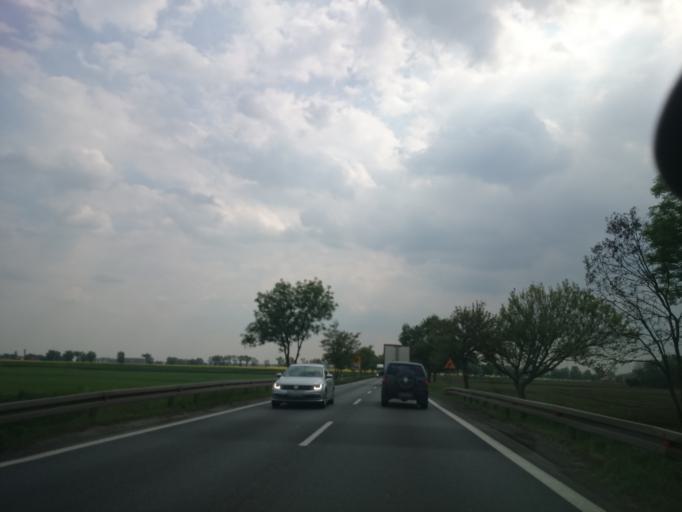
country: PL
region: Lower Silesian Voivodeship
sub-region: Powiat wroclawski
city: Kobierzyce
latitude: 50.9775
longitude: 16.9460
